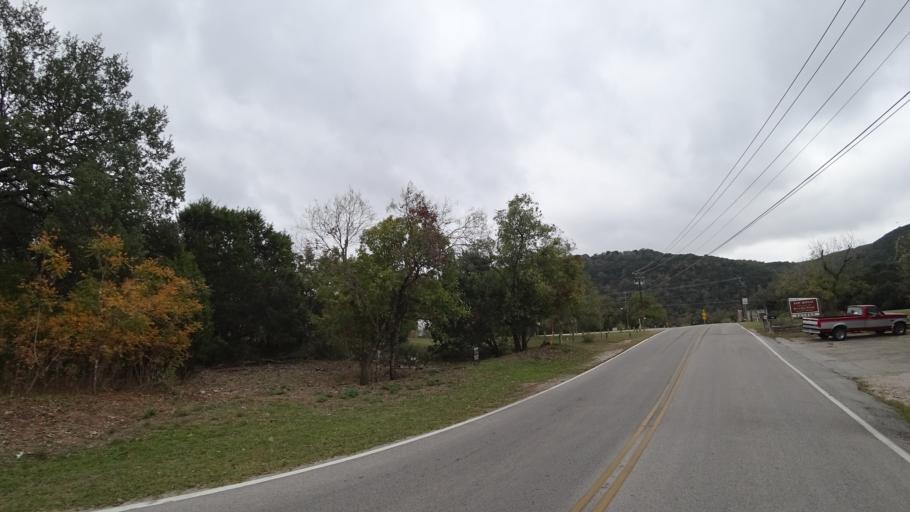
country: US
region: Texas
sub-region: Travis County
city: Bee Cave
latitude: 30.3293
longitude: -97.9264
